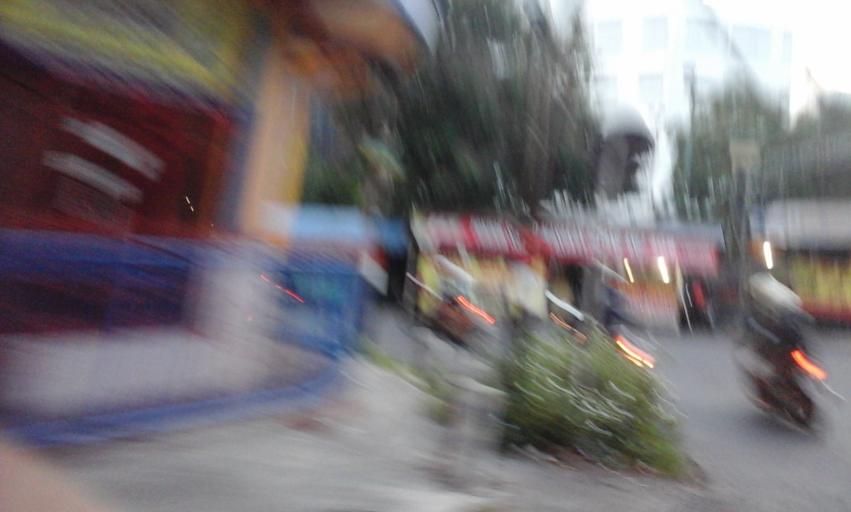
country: ID
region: East Java
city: Jember
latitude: -8.1688
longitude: 113.7041
